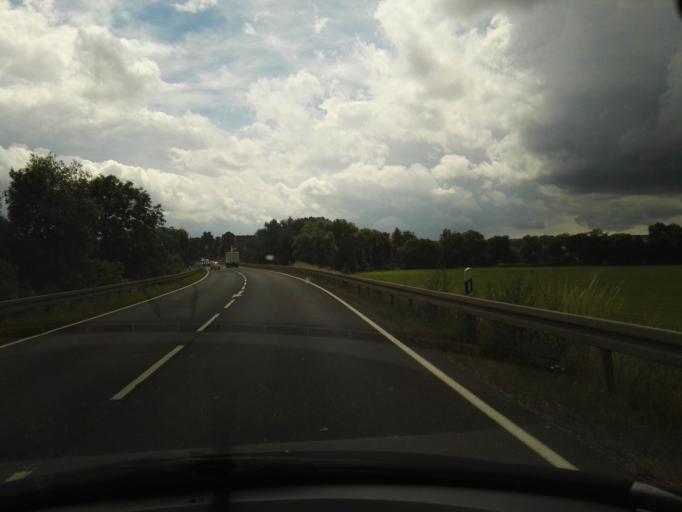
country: DE
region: Bavaria
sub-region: Upper Franconia
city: Hochstadt am Main
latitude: 50.1572
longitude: 11.1795
